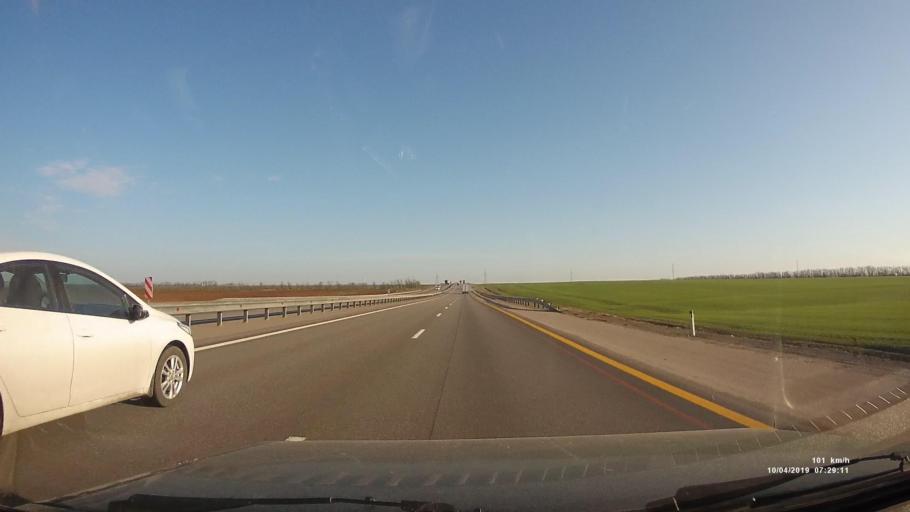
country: RU
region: Rostov
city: Zverevo
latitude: 47.9512
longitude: 40.2179
